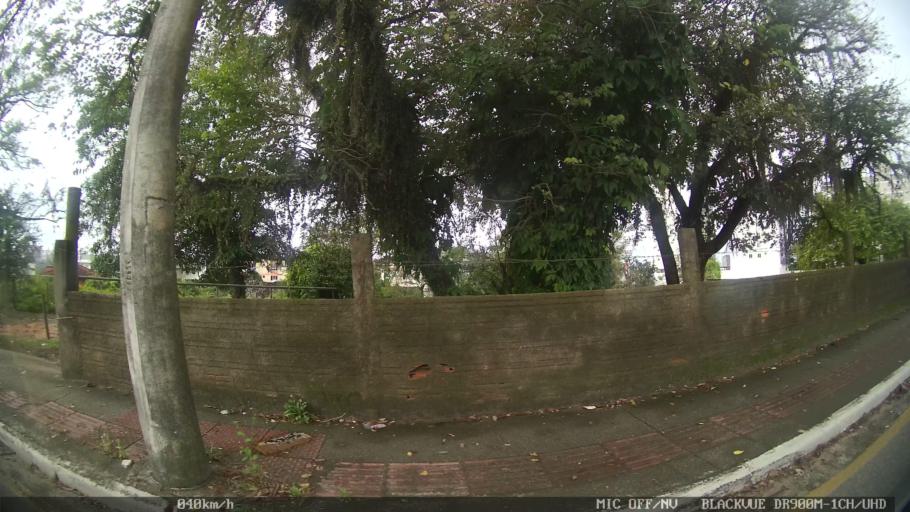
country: BR
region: Santa Catarina
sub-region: Sao Jose
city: Campinas
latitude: -27.5888
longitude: -48.6209
